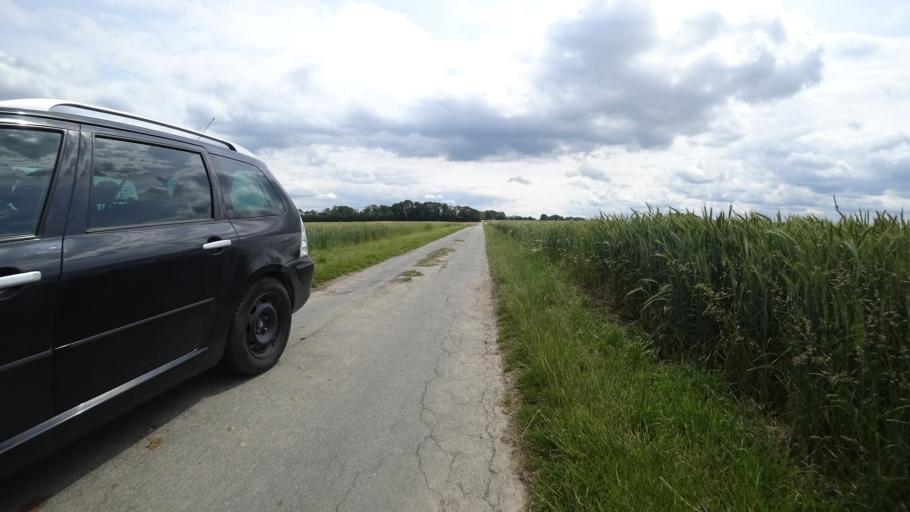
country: DE
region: North Rhine-Westphalia
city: Erwitte
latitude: 51.6093
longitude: 8.3952
